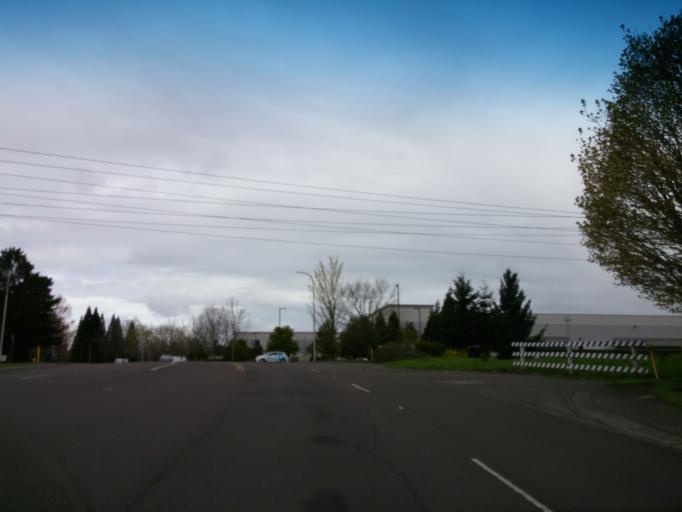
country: US
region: Oregon
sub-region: Washington County
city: Cedar Mill
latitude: 45.5250
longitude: -122.8270
